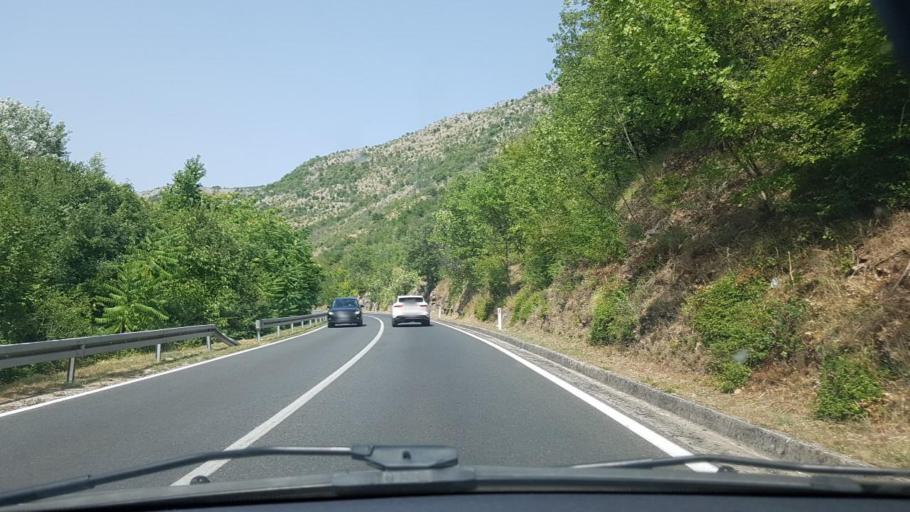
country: BA
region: Federation of Bosnia and Herzegovina
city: Tasovcici
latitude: 43.1700
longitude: 17.7853
